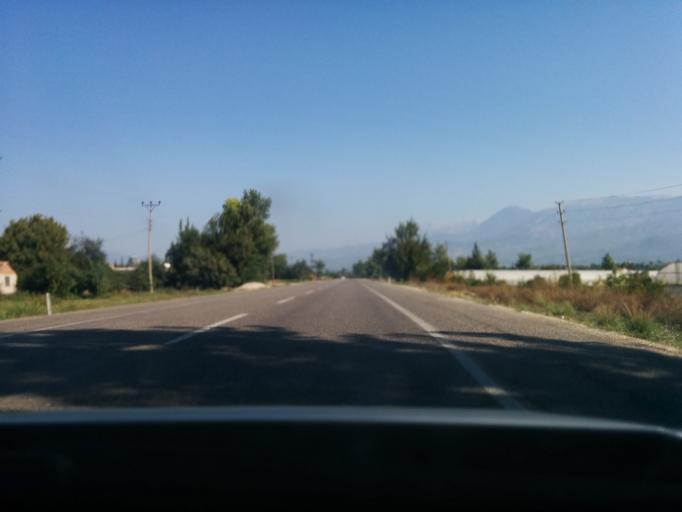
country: TR
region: Mugla
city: Esen
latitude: 36.5109
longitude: 29.3342
